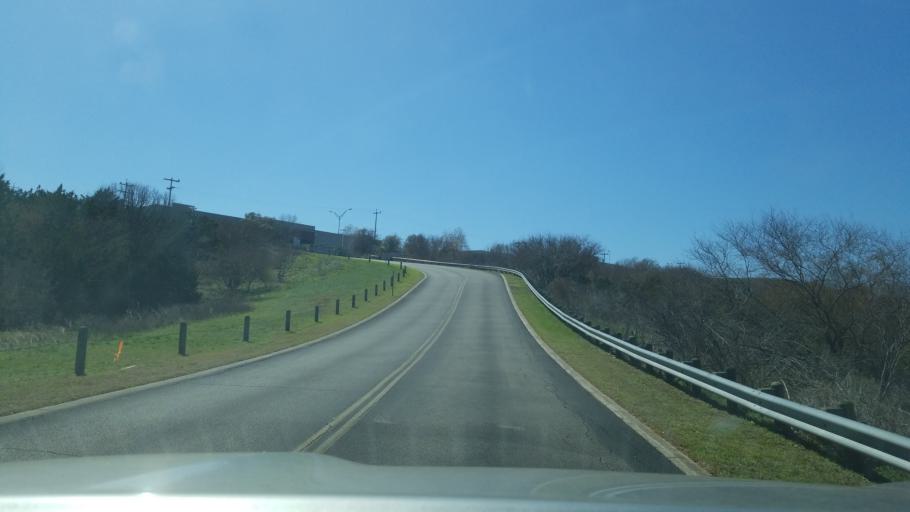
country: US
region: Texas
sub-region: Bexar County
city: Hollywood Park
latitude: 29.6094
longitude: -98.4577
